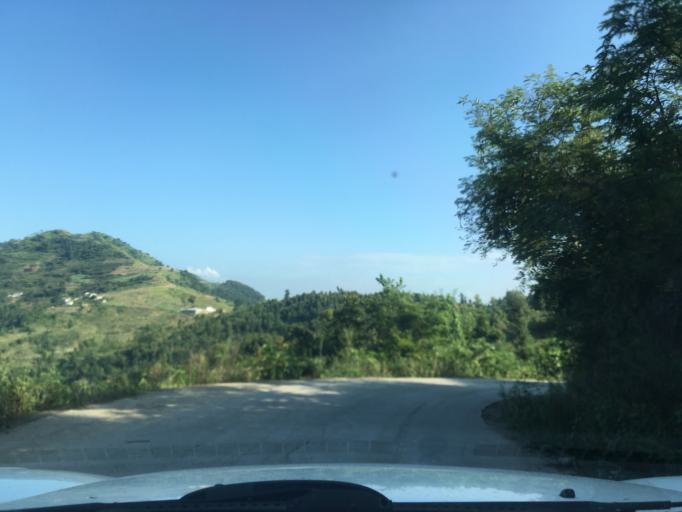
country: CN
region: Guangxi Zhuangzu Zizhiqu
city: Xinzhou
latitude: 25.4274
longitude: 105.7474
